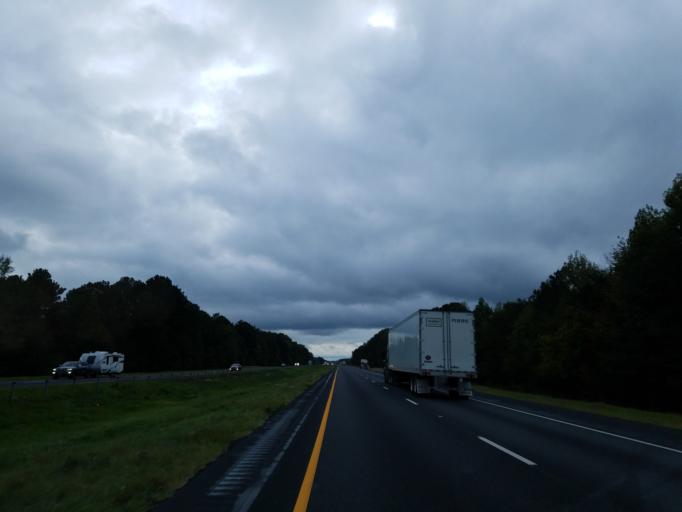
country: US
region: Alabama
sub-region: Sumter County
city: Livingston
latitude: 32.7251
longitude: -88.1144
